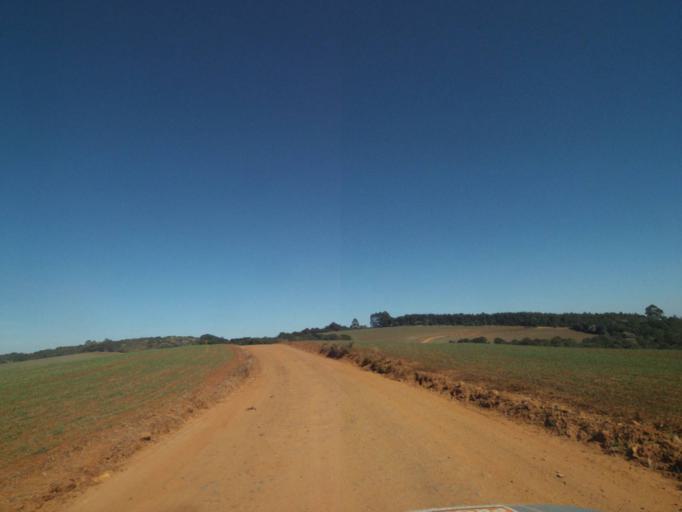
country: BR
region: Parana
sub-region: Tibagi
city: Tibagi
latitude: -24.5645
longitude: -50.6262
